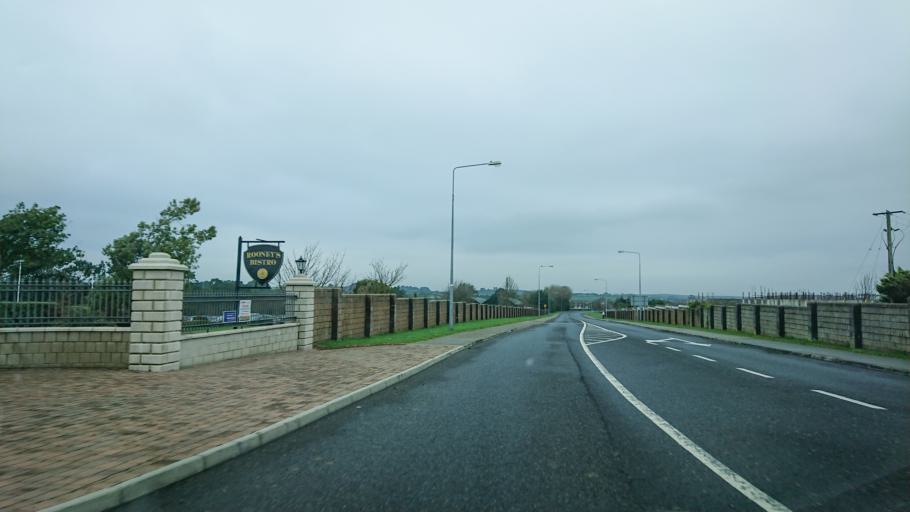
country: IE
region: Munster
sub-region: Waterford
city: Tra Mhor
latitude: 52.1555
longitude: -7.1698
